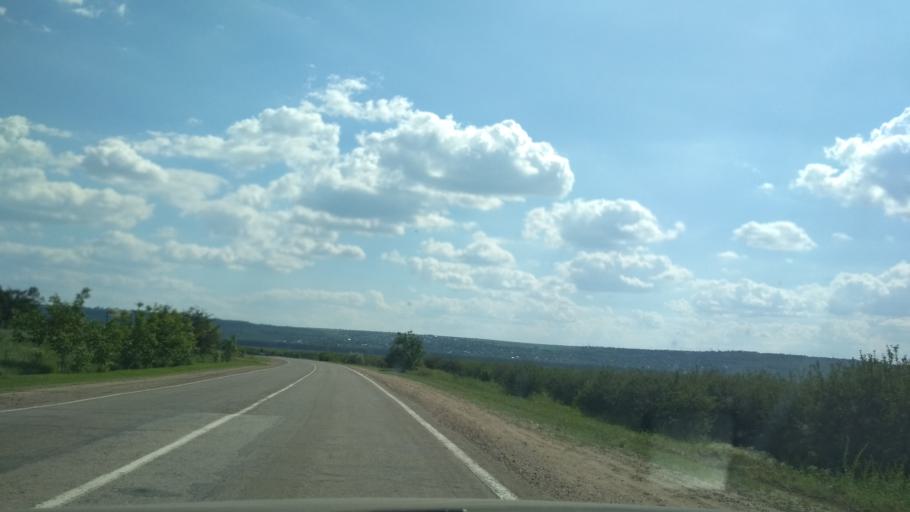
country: MD
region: Chisinau
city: Vadul lui Voda
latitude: 47.1149
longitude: 29.1059
